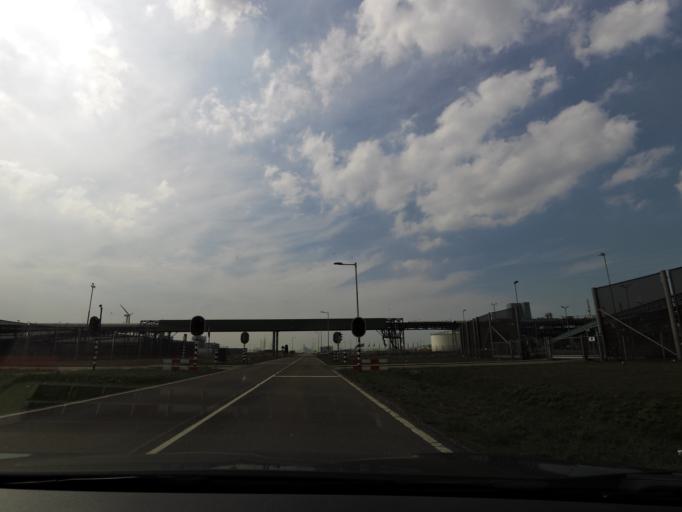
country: NL
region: South Holland
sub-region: Gemeente Rotterdam
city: Hoek van Holland
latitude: 51.9562
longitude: 4.1033
